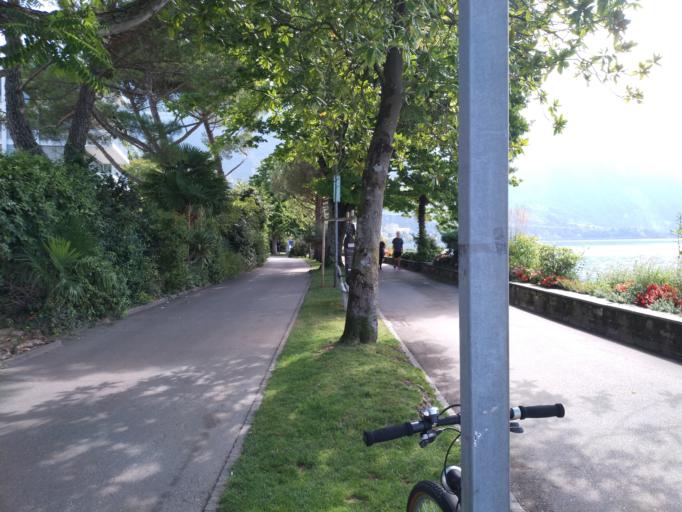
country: CH
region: Vaud
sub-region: Riviera-Pays-d'Enhaut District
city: Montreux
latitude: 46.4290
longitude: 6.9116
